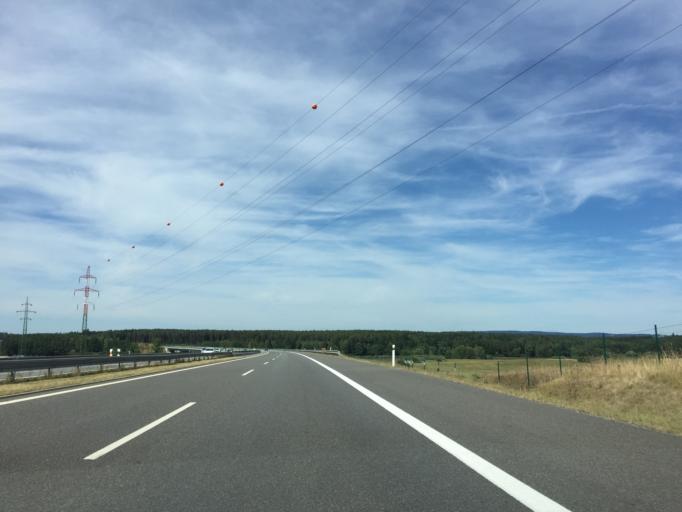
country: CZ
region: Jihocesky
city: Plana nad Luznici
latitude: 49.3314
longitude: 14.7377
